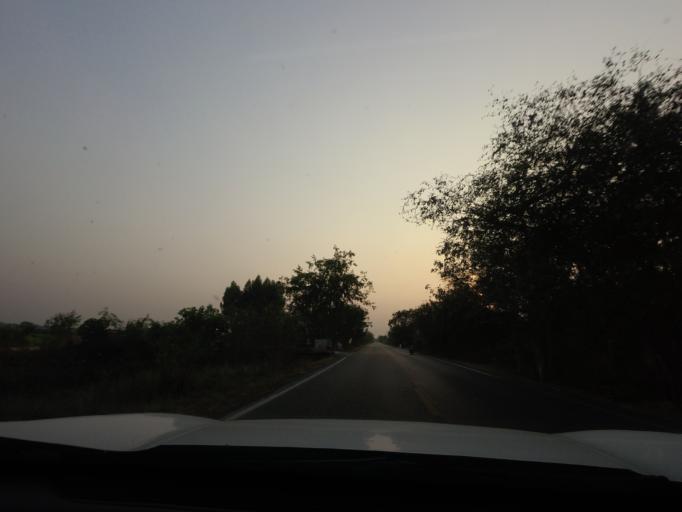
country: TH
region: Nakhon Nayok
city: Ongkharak
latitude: 14.1521
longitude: 101.0391
